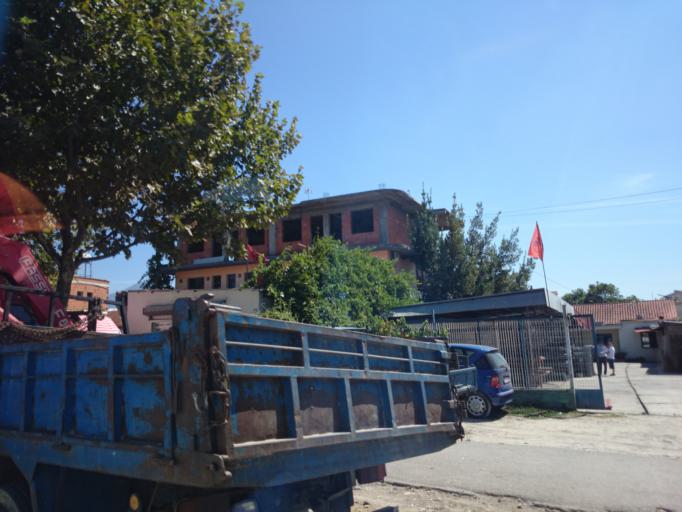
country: AL
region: Tirane
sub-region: Rrethi i Tiranes
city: Paskuqan
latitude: 41.3377
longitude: 19.7850
